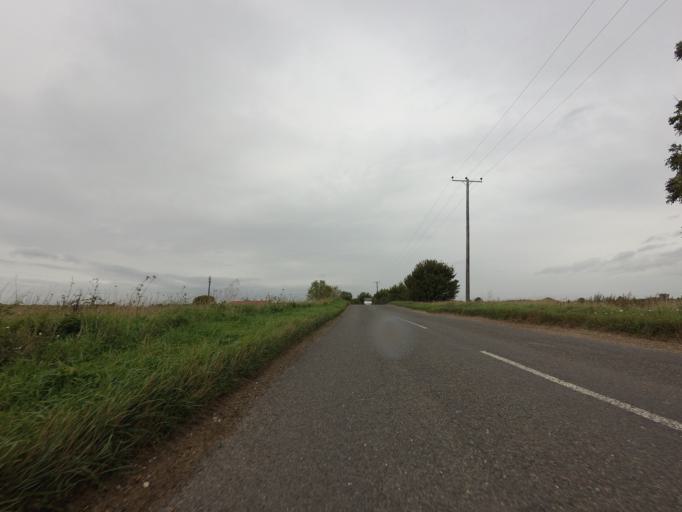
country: GB
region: England
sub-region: Cambridgeshire
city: Harston
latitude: 52.0803
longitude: 0.0829
